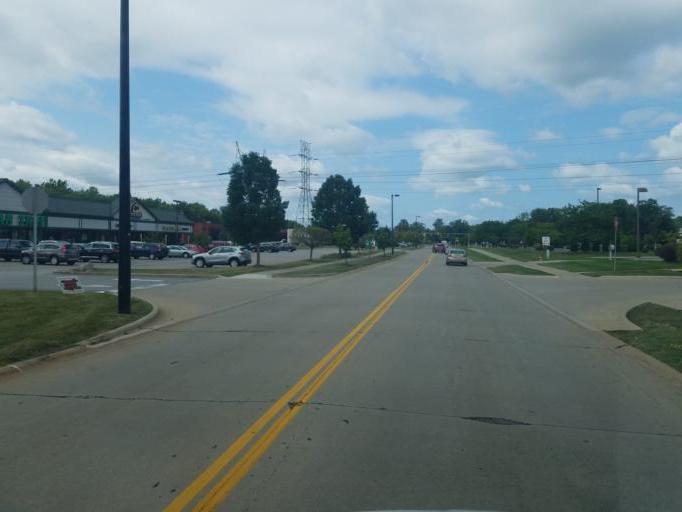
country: US
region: Ohio
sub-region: Lake County
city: Fairport Harbor
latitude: 41.7147
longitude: -81.2949
